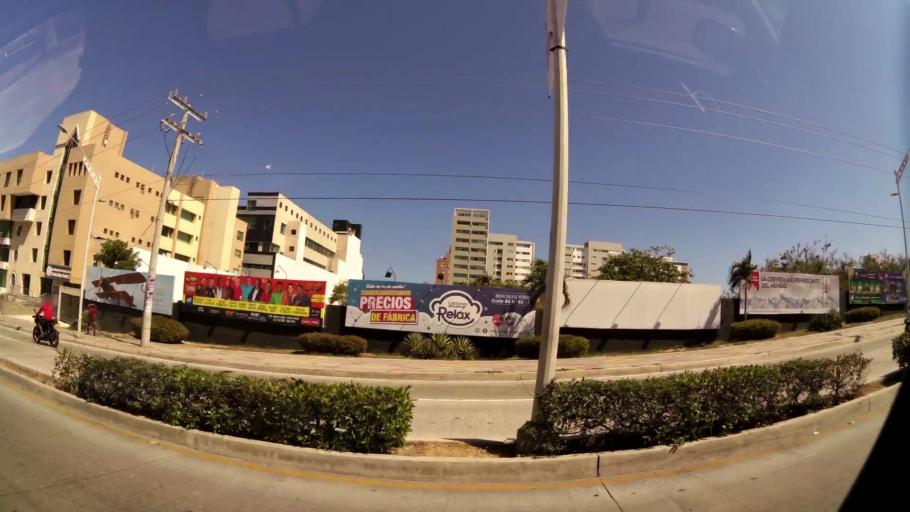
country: CO
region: Atlantico
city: Barranquilla
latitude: 11.0106
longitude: -74.8278
